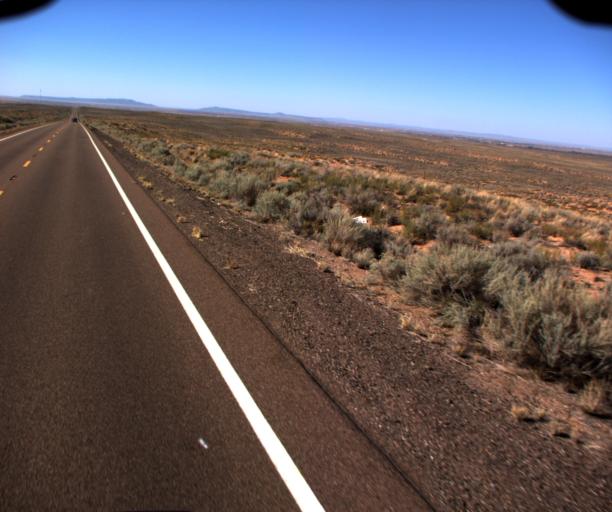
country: US
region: Arizona
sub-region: Navajo County
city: Winslow
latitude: 35.0512
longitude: -110.5964
